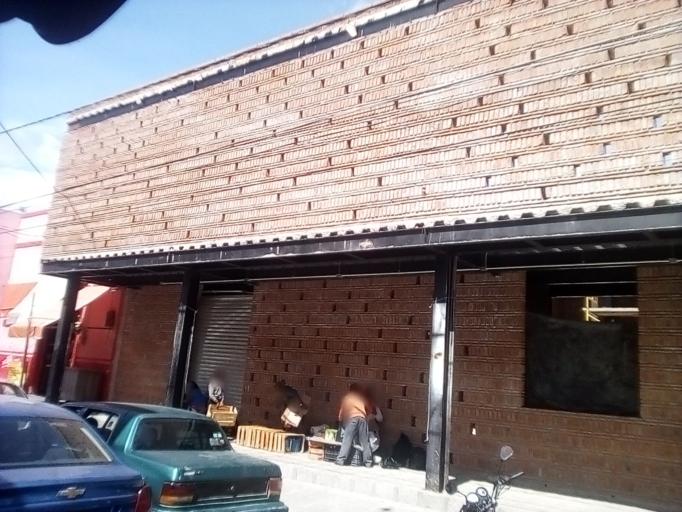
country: MX
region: Guanajuato
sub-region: San Luis de la Paz
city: San Luis de la Paz
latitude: 21.2987
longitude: -100.5168
